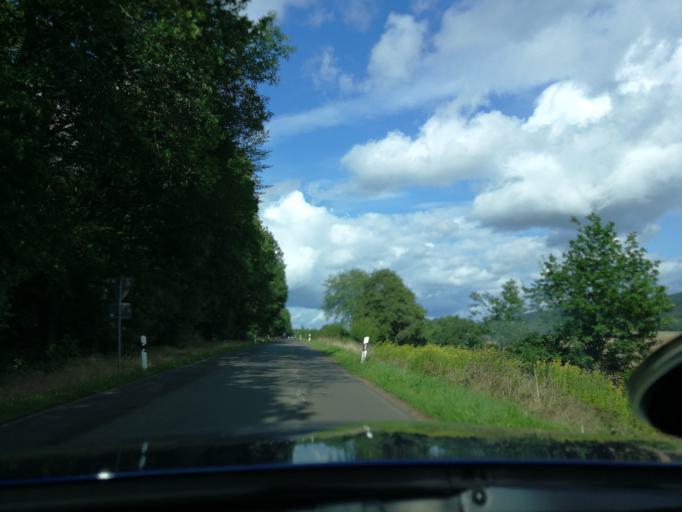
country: DE
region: Rheinland-Pfalz
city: Klausen
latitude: 49.9179
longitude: 6.8706
